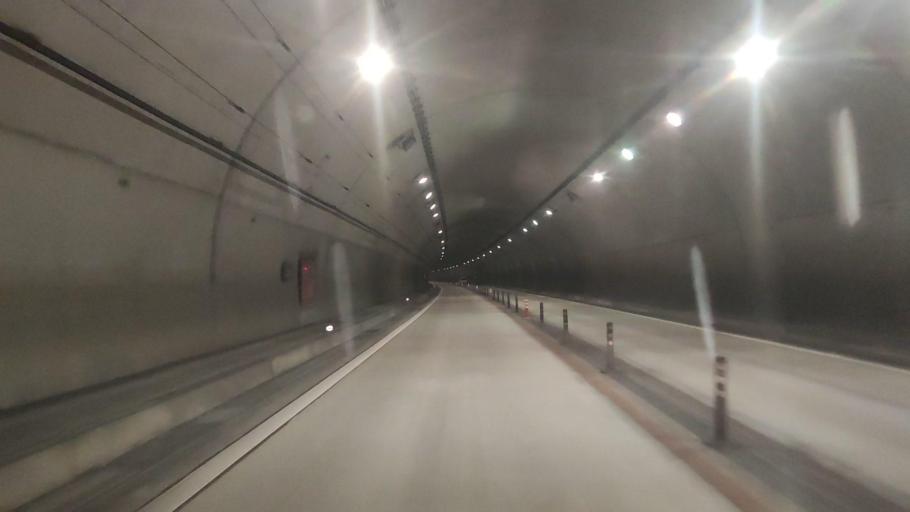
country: JP
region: Nagasaki
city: Shimabara
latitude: 32.7773
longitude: 130.3560
